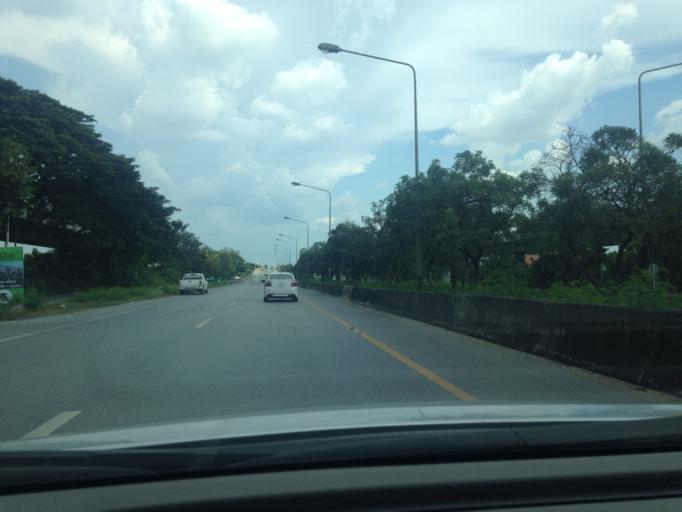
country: TH
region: Pathum Thani
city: Khlong Luang
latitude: 14.0660
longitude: 100.5850
